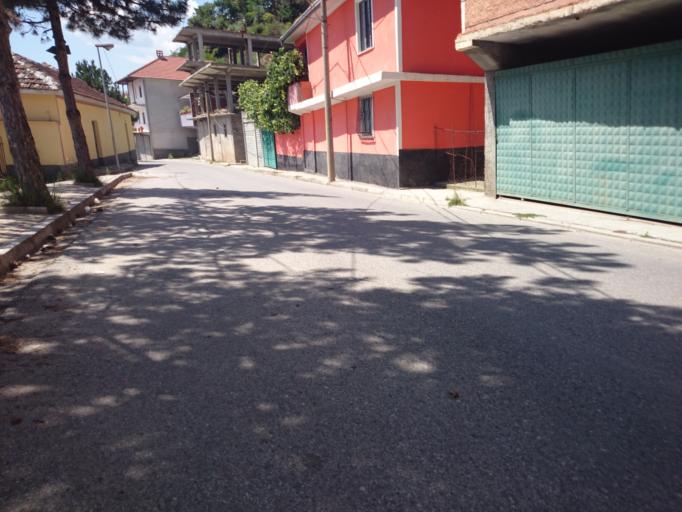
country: AL
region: Diber
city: Peshkopi
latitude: 41.6863
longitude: 20.4384
